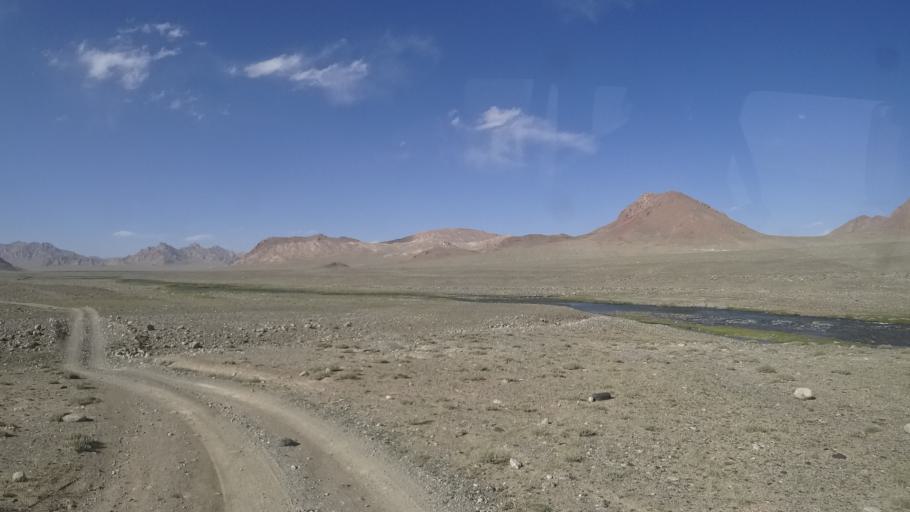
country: TJ
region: Gorno-Badakhshan
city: Murghob
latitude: 37.5800
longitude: 74.1574
